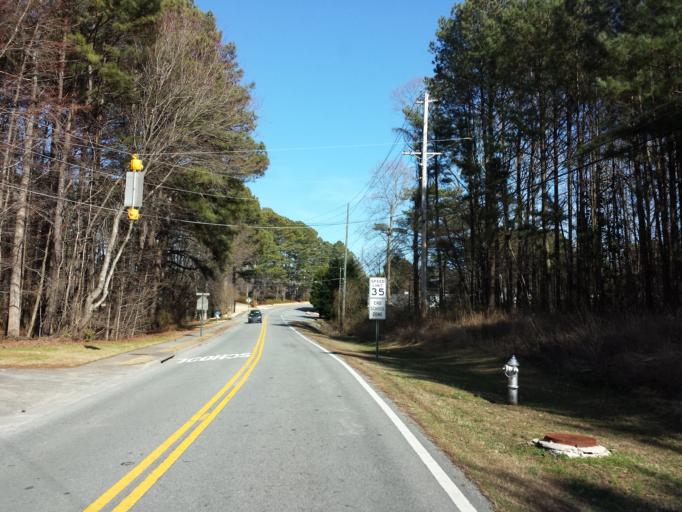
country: US
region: Georgia
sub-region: Cobb County
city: Kennesaw
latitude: 34.0285
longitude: -84.5953
